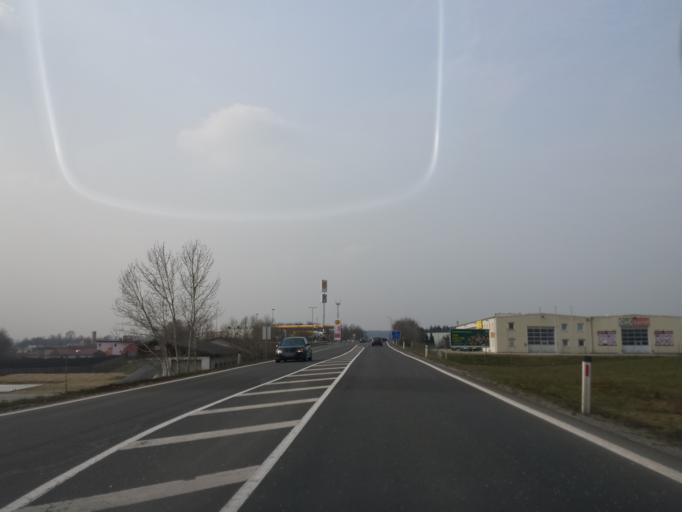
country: AT
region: Styria
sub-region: Politischer Bezirk Suedoststeiermark
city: Breitenfeld an der Rittschein
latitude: 47.0784
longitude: 15.9651
